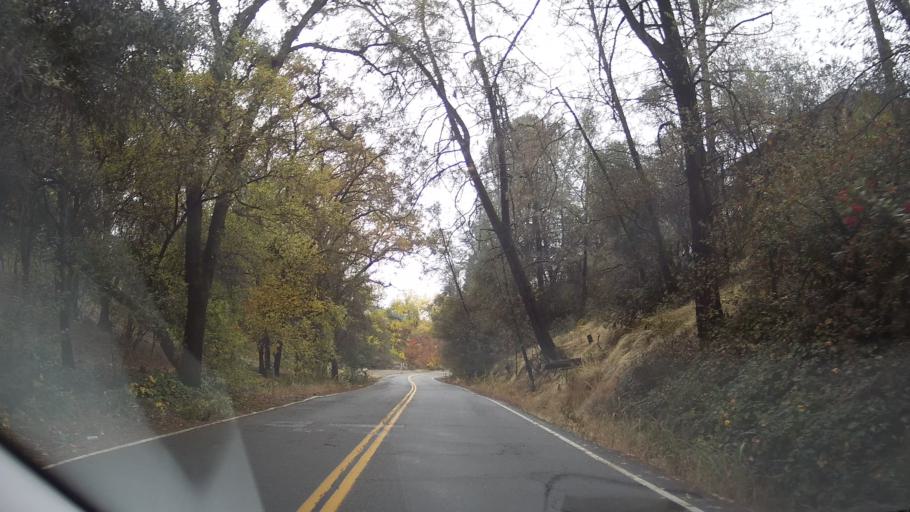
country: US
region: California
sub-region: Placer County
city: North Auburn
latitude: 38.9151
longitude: -121.0773
